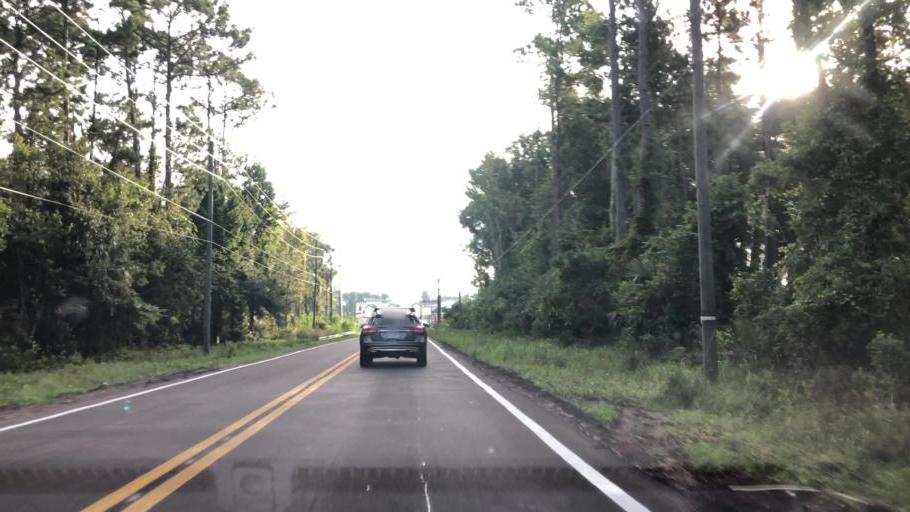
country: US
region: Florida
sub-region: Saint Johns County
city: Palm Valley
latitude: 30.1190
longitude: -81.4109
